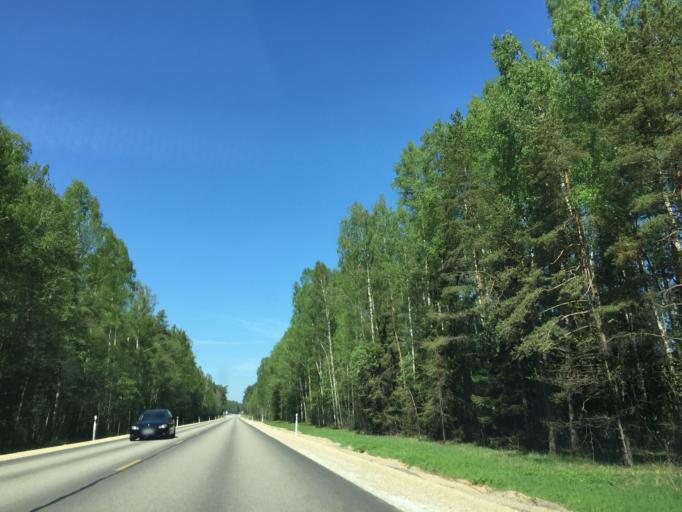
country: LV
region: Salaspils
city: Salaspils
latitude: 56.9133
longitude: 24.4023
